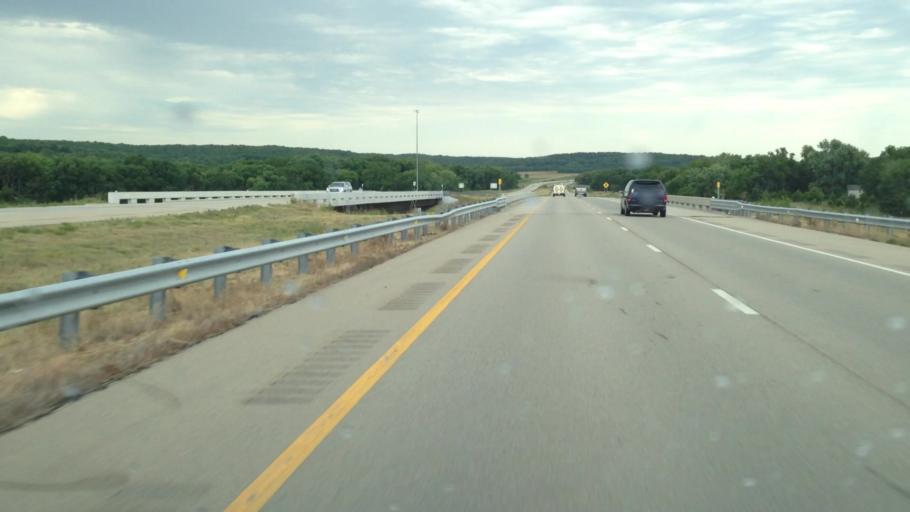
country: US
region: Kansas
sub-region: Douglas County
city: Lawrence
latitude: 38.8854
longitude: -95.2588
